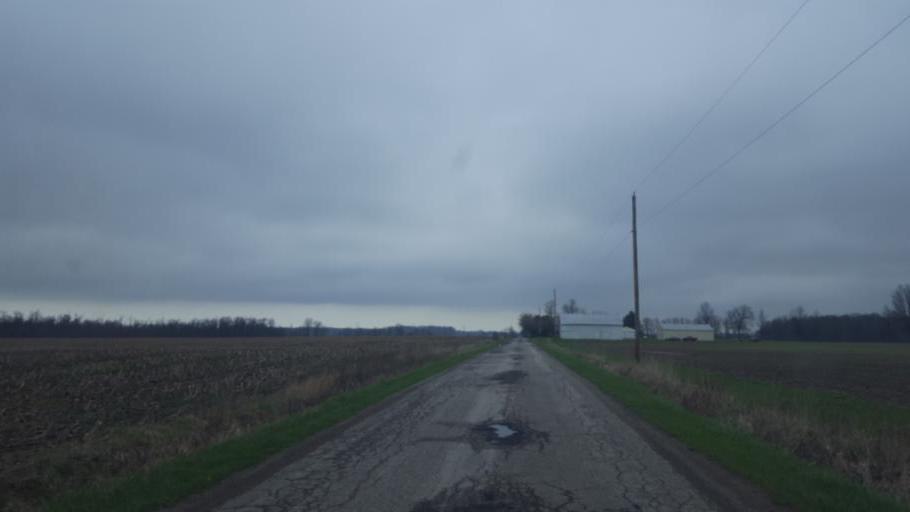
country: US
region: Ohio
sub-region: Crawford County
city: Galion
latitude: 40.6979
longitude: -82.7462
